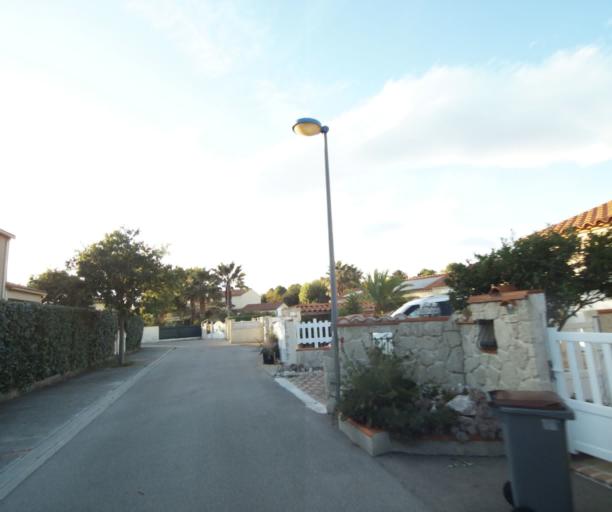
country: FR
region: Languedoc-Roussillon
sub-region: Departement des Pyrenees-Orientales
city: Argelers
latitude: 42.5696
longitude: 3.0072
